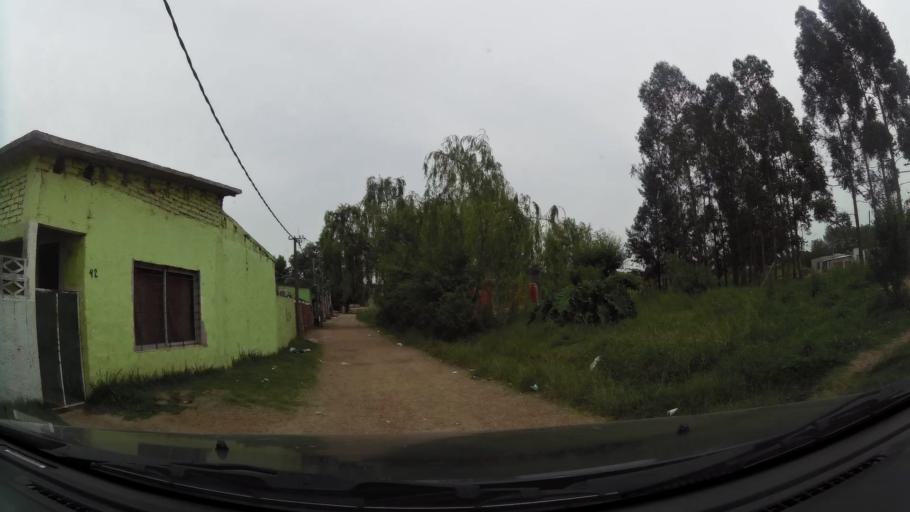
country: UY
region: Canelones
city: Las Piedras
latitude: -34.7438
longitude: -56.2189
